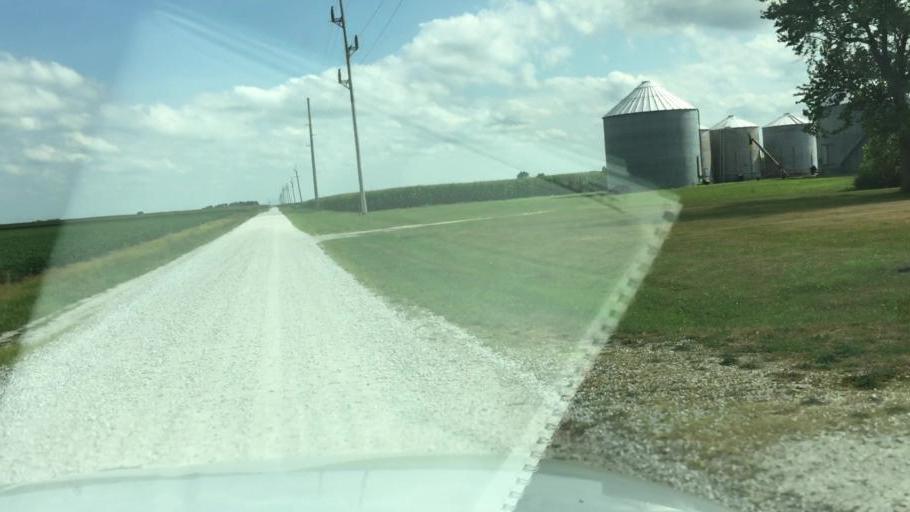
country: US
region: Illinois
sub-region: Hancock County
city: Carthage
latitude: 40.4161
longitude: -91.1784
